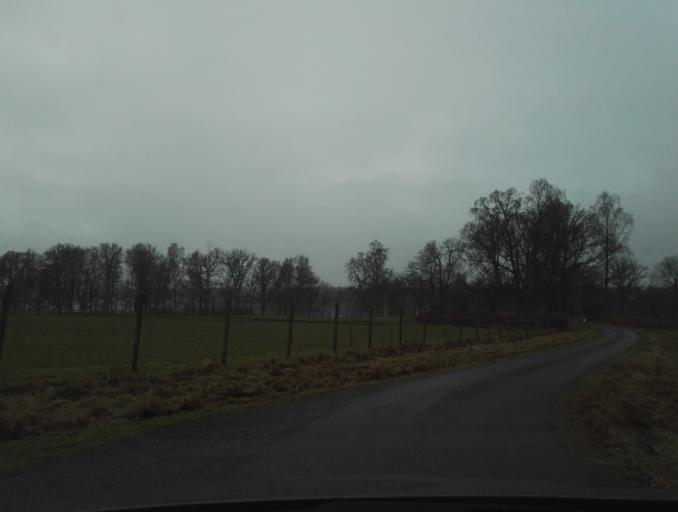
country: SE
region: Kronoberg
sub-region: Vaxjo Kommun
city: Vaexjoe
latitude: 56.9424
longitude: 14.7647
